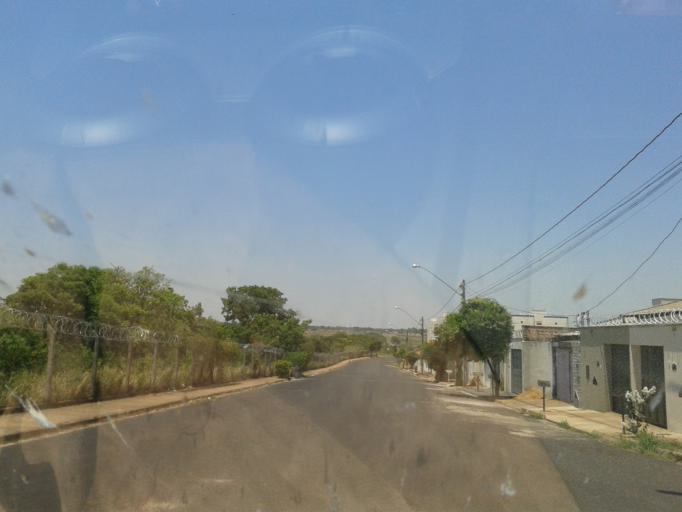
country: BR
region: Minas Gerais
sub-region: Uberlandia
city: Uberlandia
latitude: -18.9624
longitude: -48.3115
